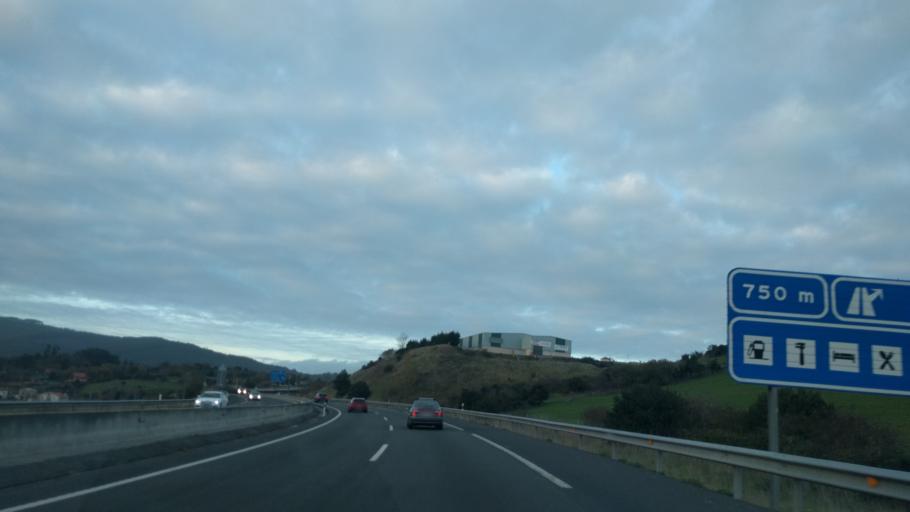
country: ES
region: Cantabria
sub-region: Provincia de Cantabria
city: Castro-Urdiales
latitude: 43.3548
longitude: -3.2160
